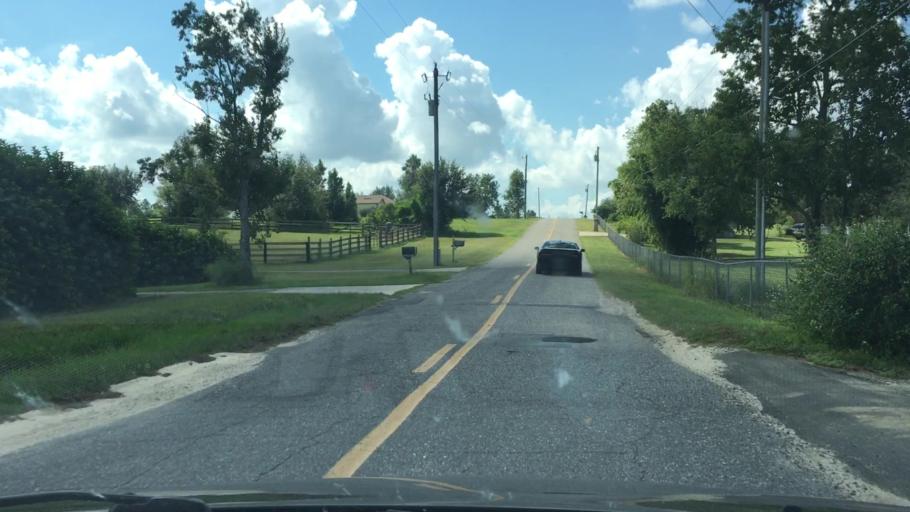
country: US
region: Florida
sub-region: Lake County
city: Minneola
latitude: 28.6405
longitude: -81.7311
